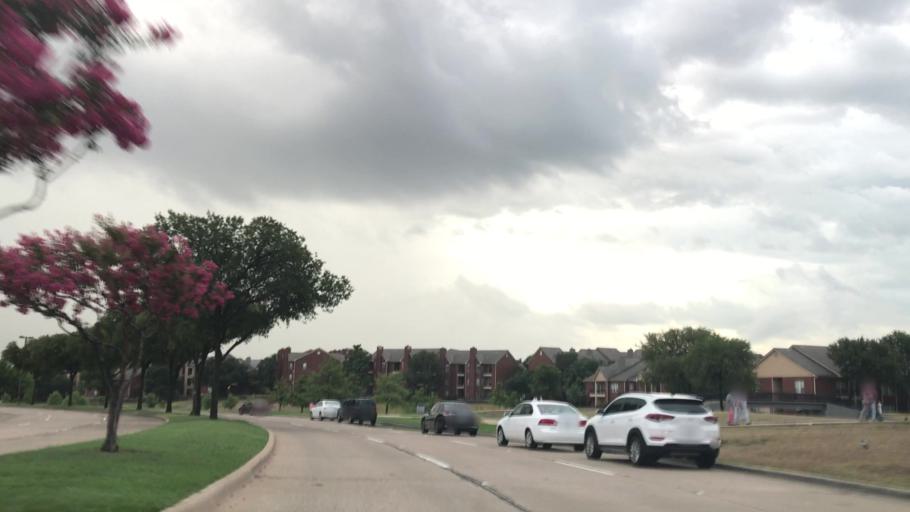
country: US
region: Texas
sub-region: Dallas County
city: Irving
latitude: 32.8806
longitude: -96.9673
